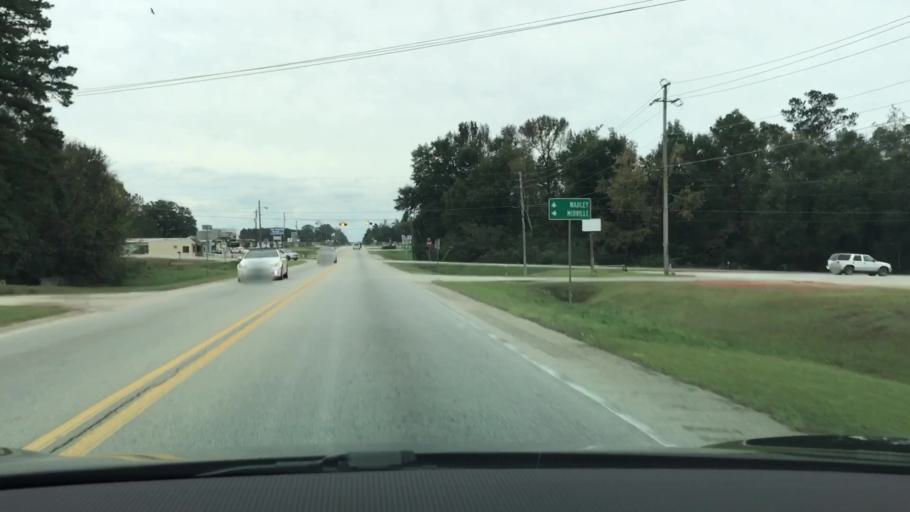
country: US
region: Georgia
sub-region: Jefferson County
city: Louisville
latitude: 32.9974
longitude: -82.3945
